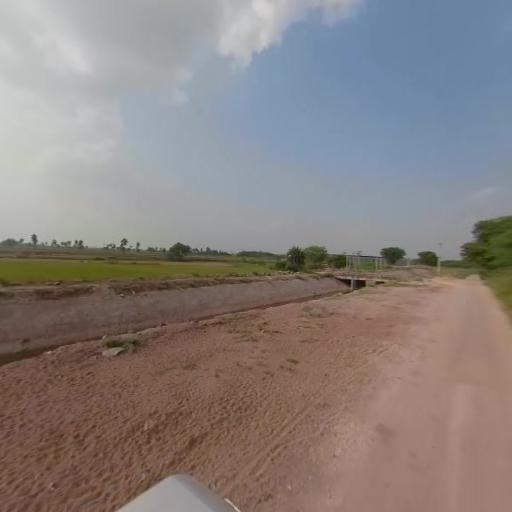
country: IN
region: Telangana
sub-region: Nalgonda
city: Suriapet
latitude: 17.1992
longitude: 79.4903
